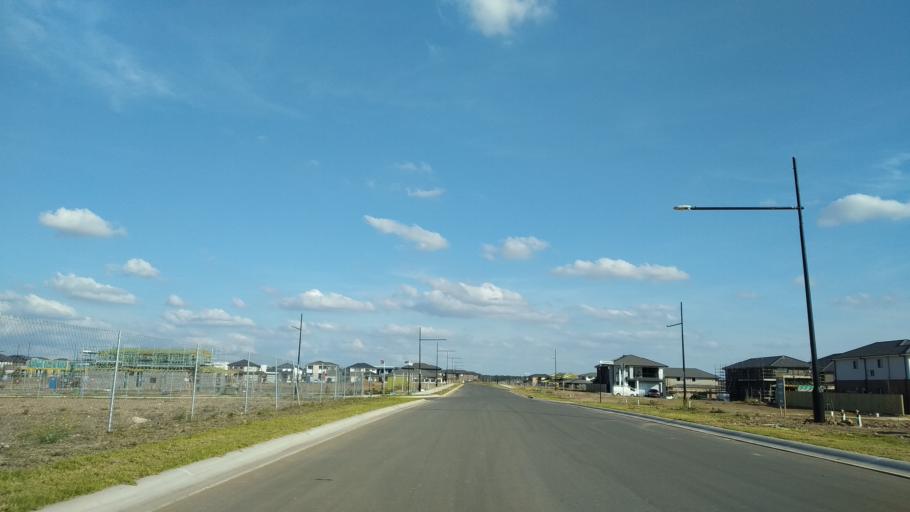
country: AU
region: New South Wales
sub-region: Blacktown
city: Blackett
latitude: -33.6894
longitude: 150.8091
